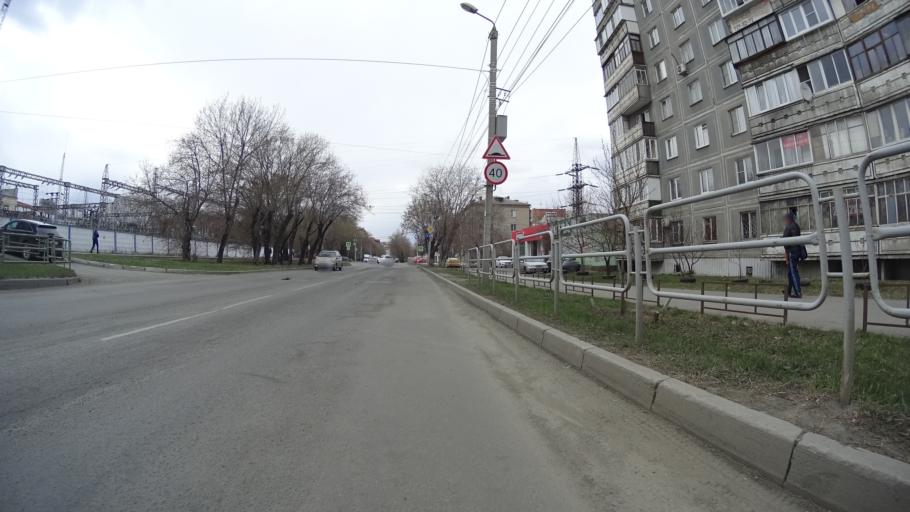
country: RU
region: Chelyabinsk
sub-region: Gorod Chelyabinsk
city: Chelyabinsk
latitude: 55.1631
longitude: 61.4215
